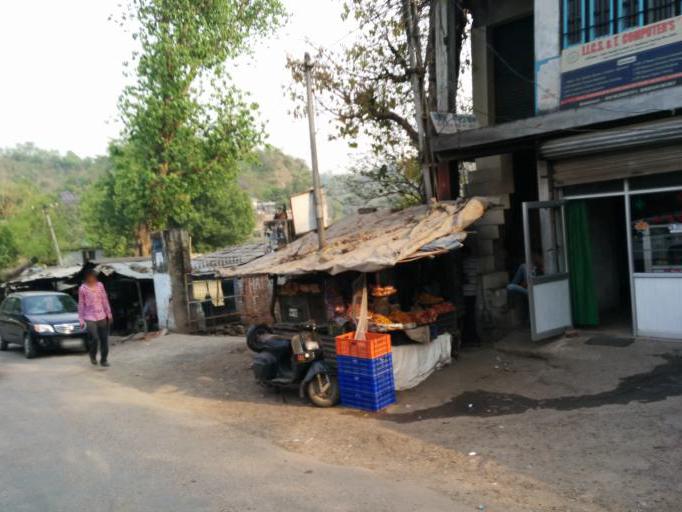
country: IN
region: Himachal Pradesh
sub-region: Kangra
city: Kotla
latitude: 32.2381
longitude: 76.0459
